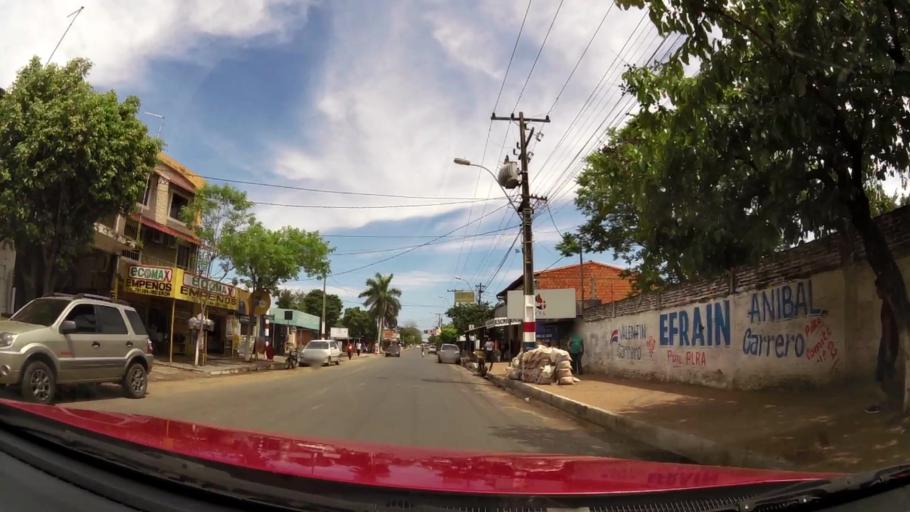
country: PY
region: Central
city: Colonia Mariano Roque Alonso
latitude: -25.2129
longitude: -57.5301
